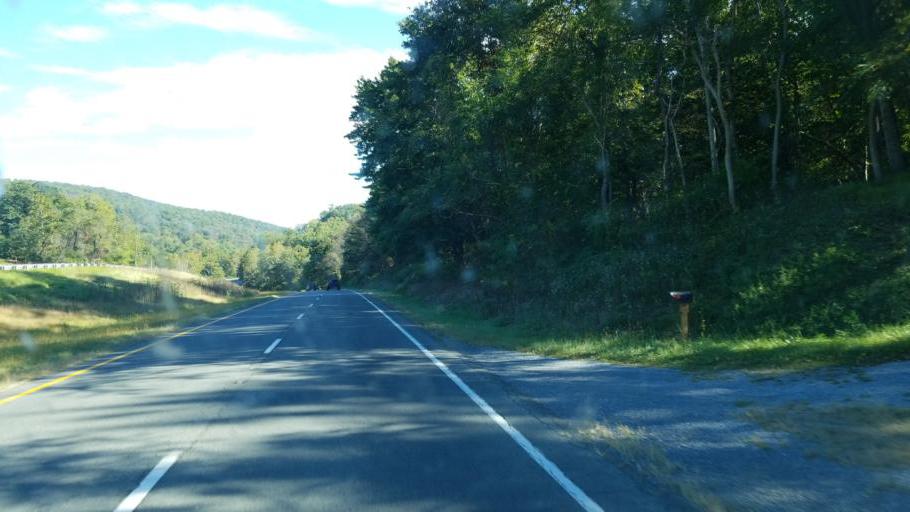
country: US
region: Virginia
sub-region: Warren County
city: Shenandoah Farms
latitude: 39.0300
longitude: -77.9831
